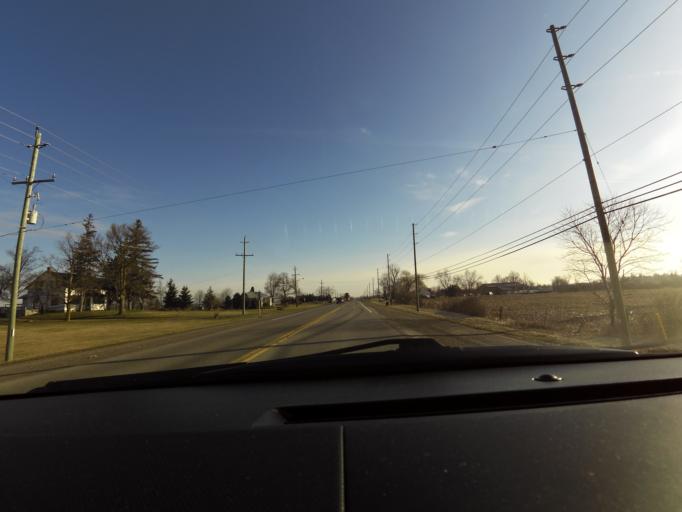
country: CA
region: Ontario
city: Ancaster
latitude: 43.0535
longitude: -79.9692
